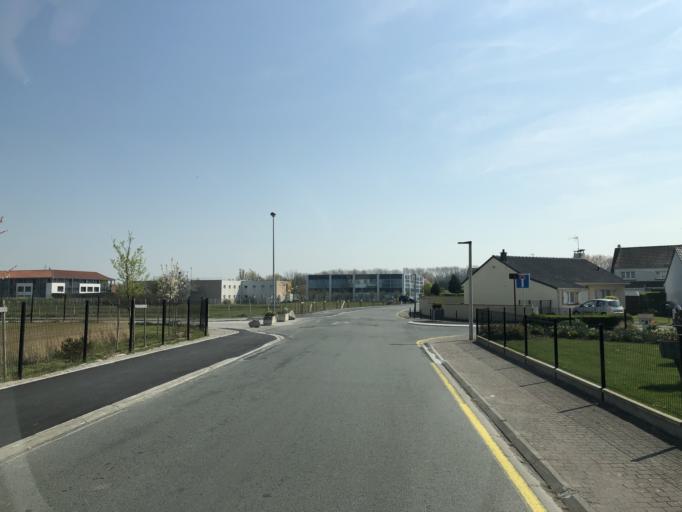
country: FR
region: Nord-Pas-de-Calais
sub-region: Departement du Pas-de-Calais
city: Coquelles
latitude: 50.9433
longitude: 1.8016
